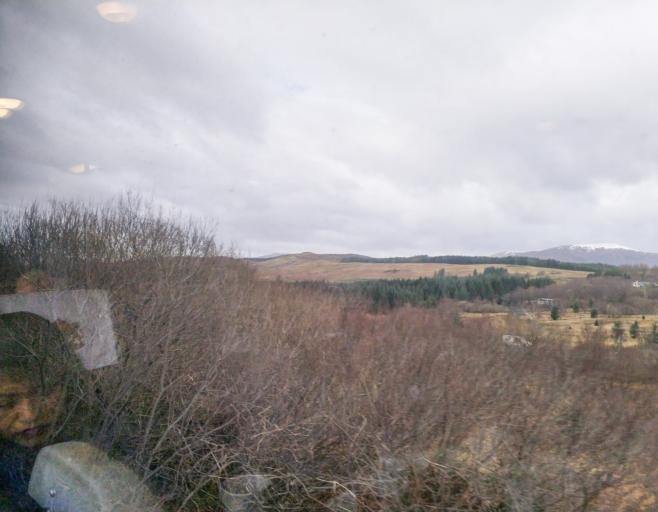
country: GB
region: Scotland
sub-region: Highland
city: Spean Bridge
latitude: 56.8818
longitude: -4.9584
